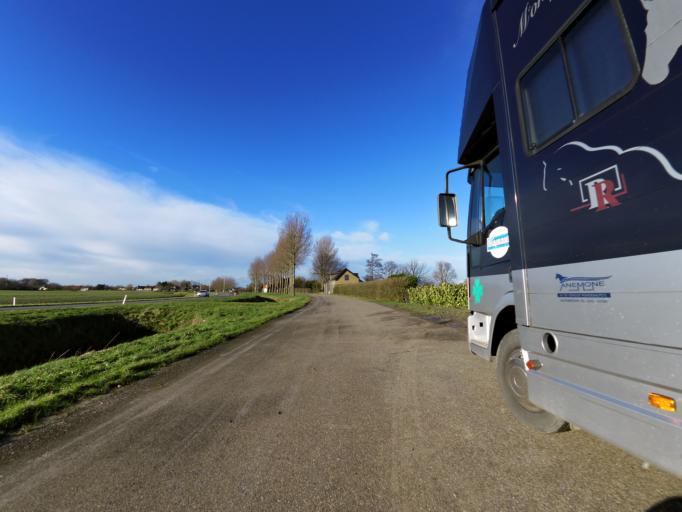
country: NL
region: South Holland
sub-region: Gemeente Hellevoetsluis
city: Nieuw-Helvoet
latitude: 51.8759
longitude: 4.0902
